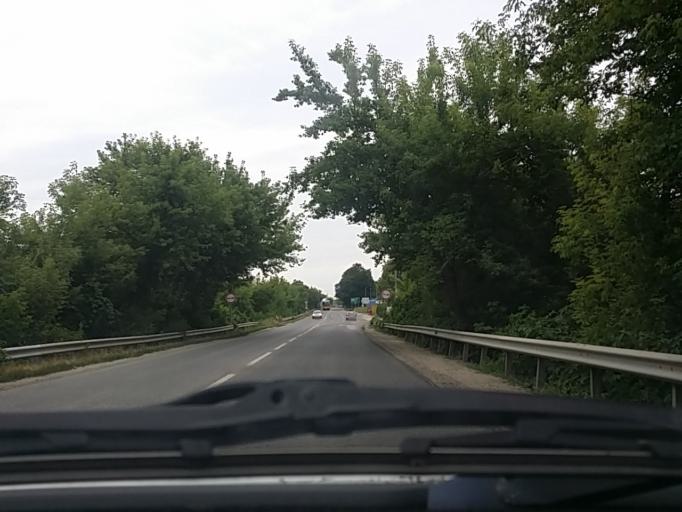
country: HU
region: Pest
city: Pilisvorosvar
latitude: 47.6141
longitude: 18.9256
